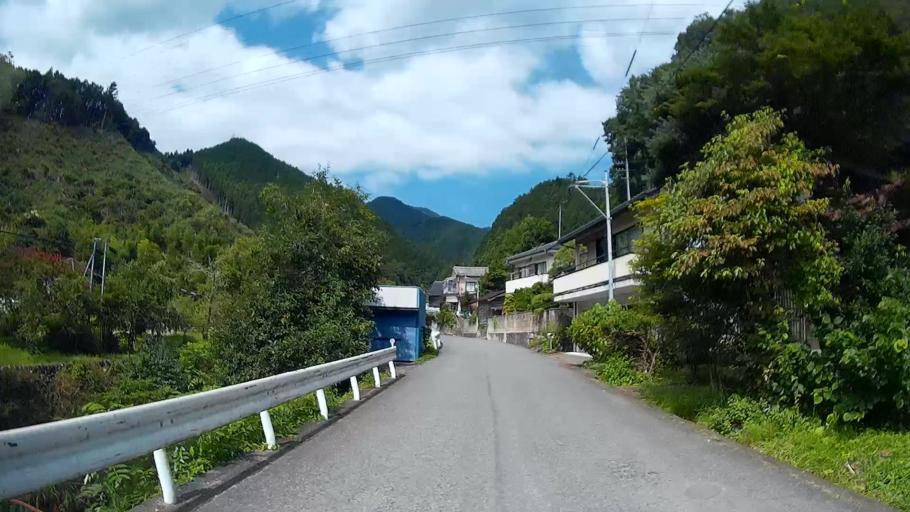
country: JP
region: Saitama
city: Chichibu
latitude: 35.9114
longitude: 139.1474
